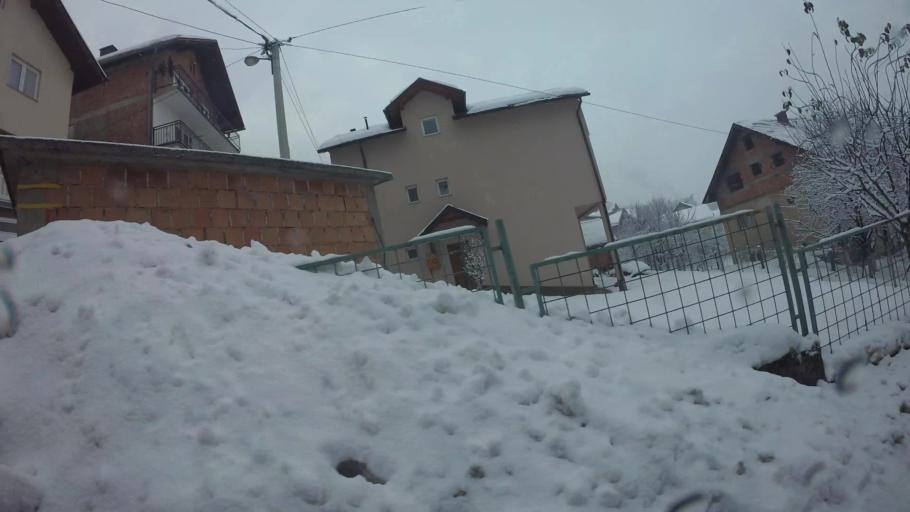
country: BA
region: Federation of Bosnia and Herzegovina
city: Kobilja Glava
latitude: 43.8465
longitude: 18.4269
